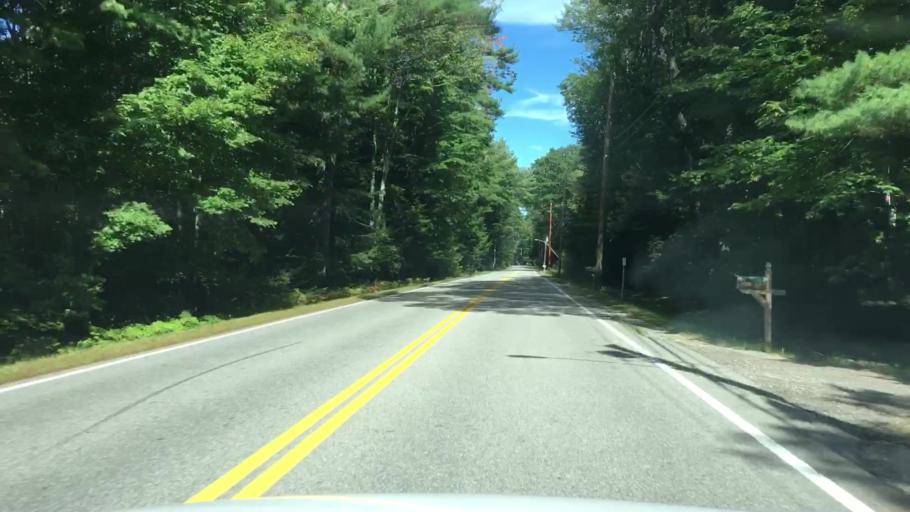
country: US
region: Maine
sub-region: Cumberland County
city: Westbrook
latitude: 43.6356
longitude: -70.4036
